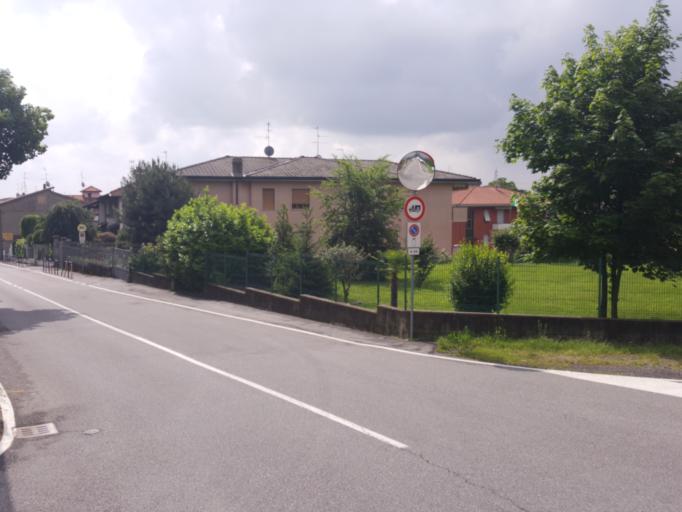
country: IT
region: Lombardy
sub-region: Provincia di Monza e Brianza
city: Giussano
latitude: 45.6845
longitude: 9.1978
